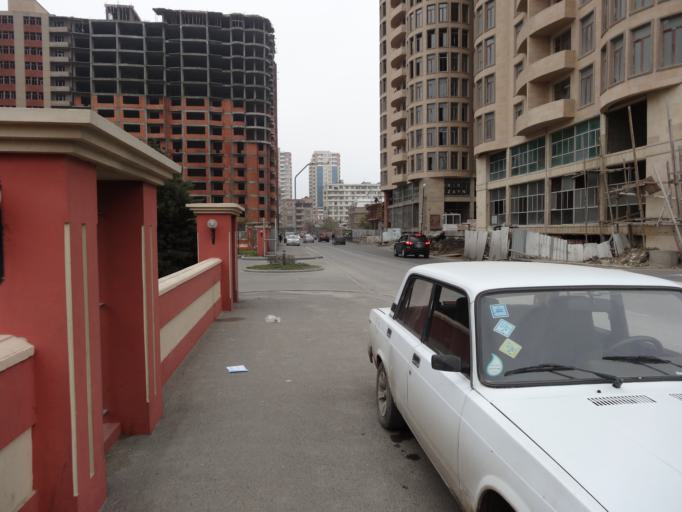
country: AZ
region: Baki
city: Baku
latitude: 40.3851
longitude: 49.8686
